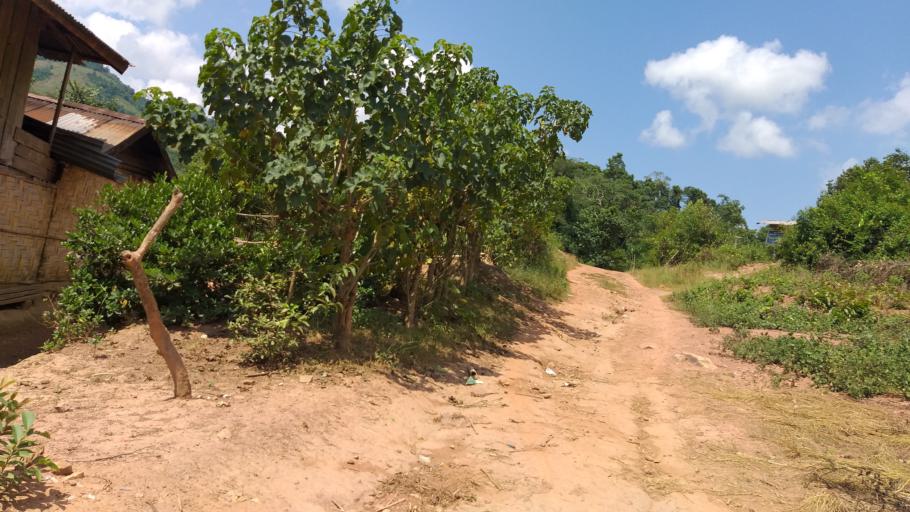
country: LA
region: Phongsali
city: Khoa
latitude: 21.3685
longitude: 102.5322
